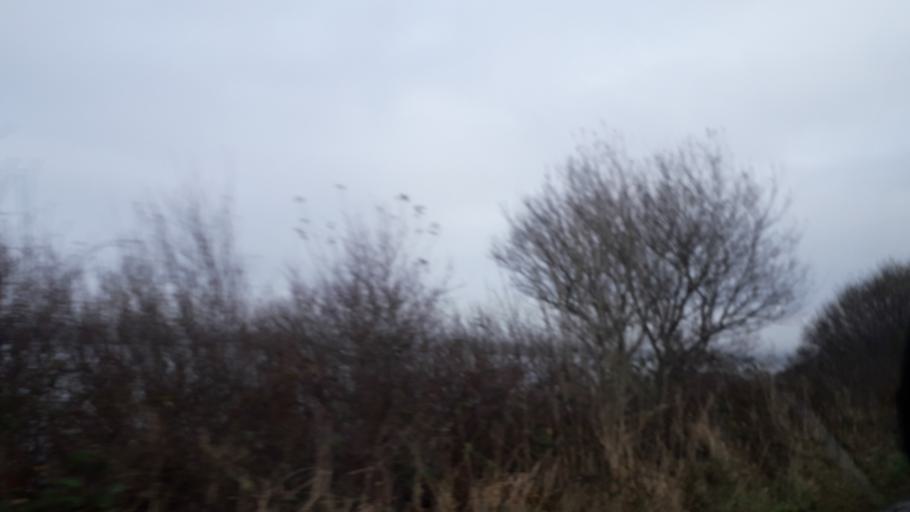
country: IE
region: Ulster
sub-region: County Donegal
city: Buncrana
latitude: 55.1656
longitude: -7.5723
